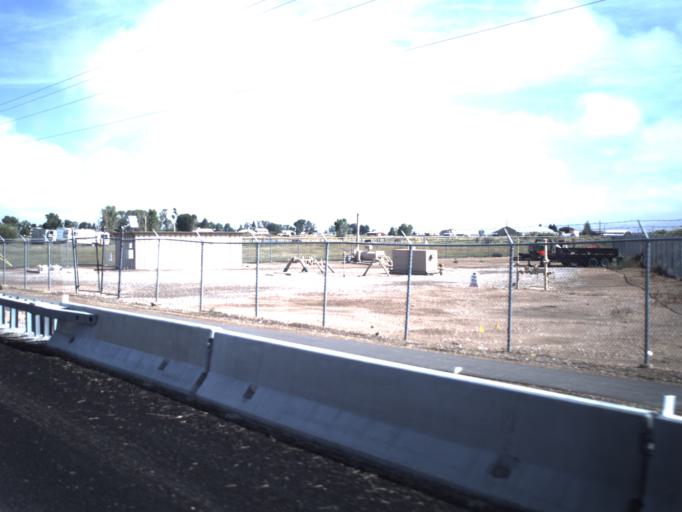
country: US
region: Utah
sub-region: Rich County
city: Randolph
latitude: 41.6577
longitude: -111.1849
